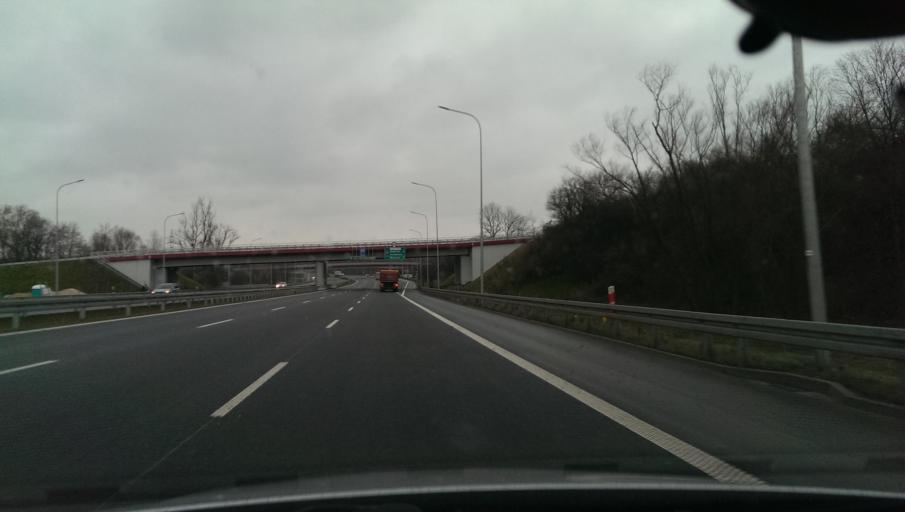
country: PL
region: Lesser Poland Voivodeship
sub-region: Powiat wielicki
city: Kokotow
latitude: 50.0556
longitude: 20.0747
